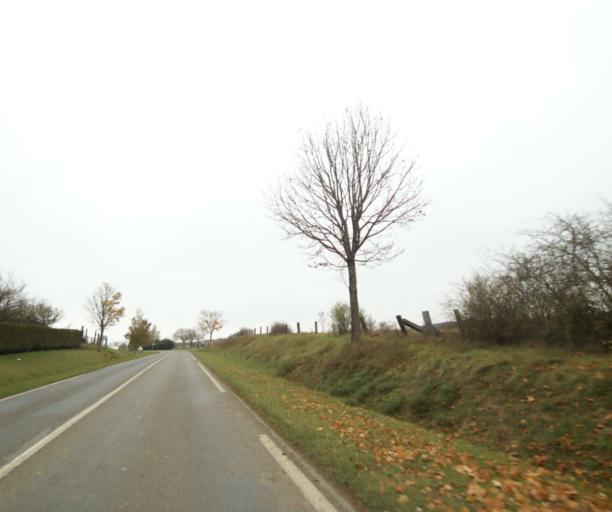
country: FR
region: Lorraine
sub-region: Departement de Meurthe-et-Moselle
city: Mancieulles
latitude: 49.2714
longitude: 5.9180
